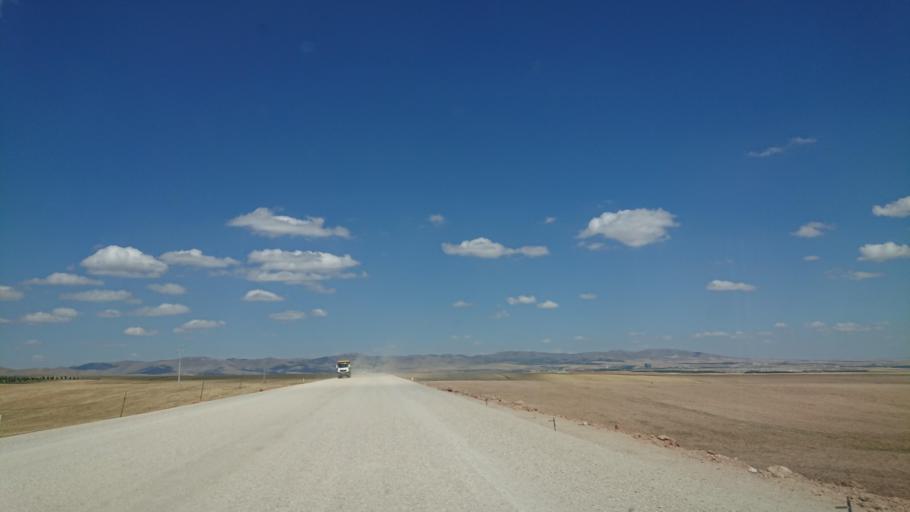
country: TR
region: Kirsehir
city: Kirsehir
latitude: 39.1355
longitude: 34.0512
